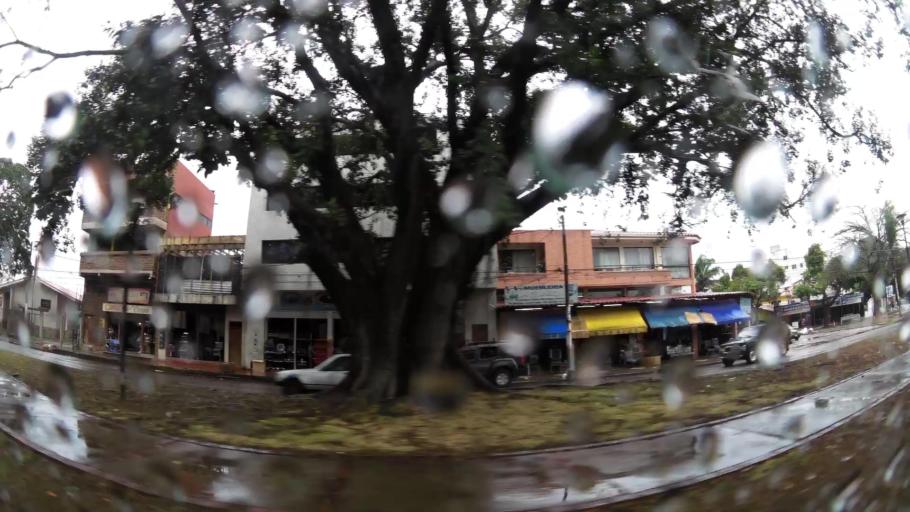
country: BO
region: Santa Cruz
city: Santa Cruz de la Sierra
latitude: -17.7860
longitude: -63.1683
